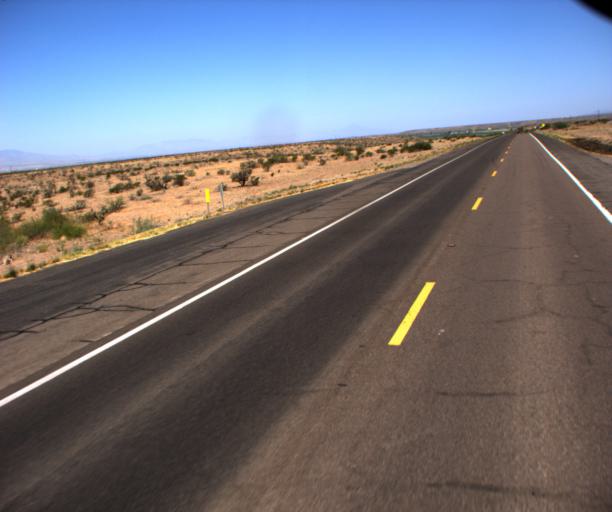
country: US
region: Arizona
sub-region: Graham County
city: Safford
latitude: 32.8078
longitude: -109.5841
